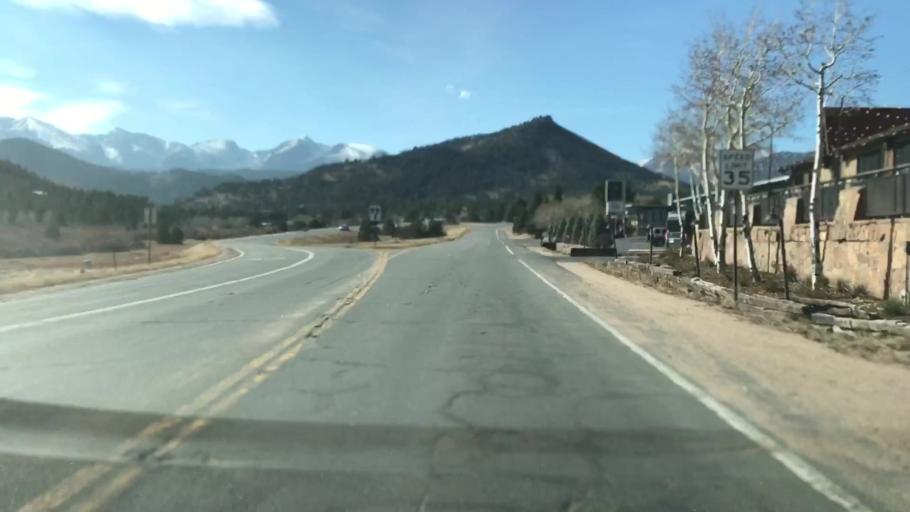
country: US
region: Colorado
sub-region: Larimer County
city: Estes Park
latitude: 40.3642
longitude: -105.5449
